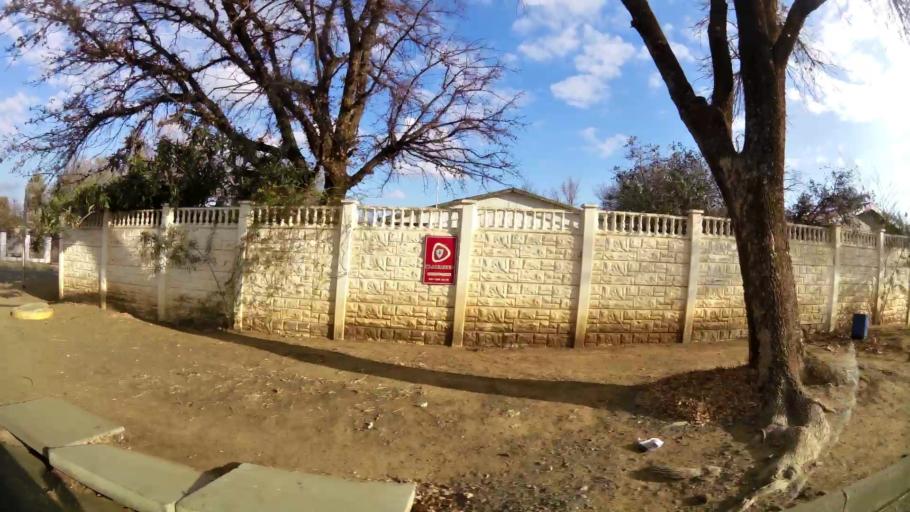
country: ZA
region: Orange Free State
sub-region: Mangaung Metropolitan Municipality
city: Bloemfontein
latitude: -29.1007
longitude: 26.1937
